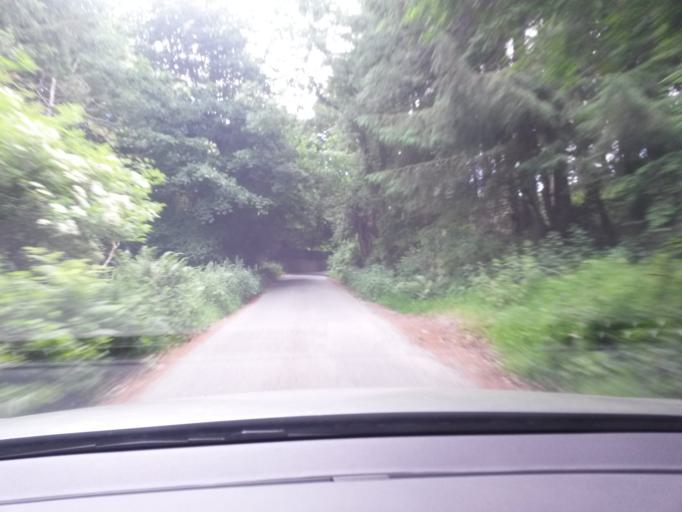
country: IE
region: Leinster
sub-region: Wicklow
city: Enniskerry
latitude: 53.1659
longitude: -6.2190
